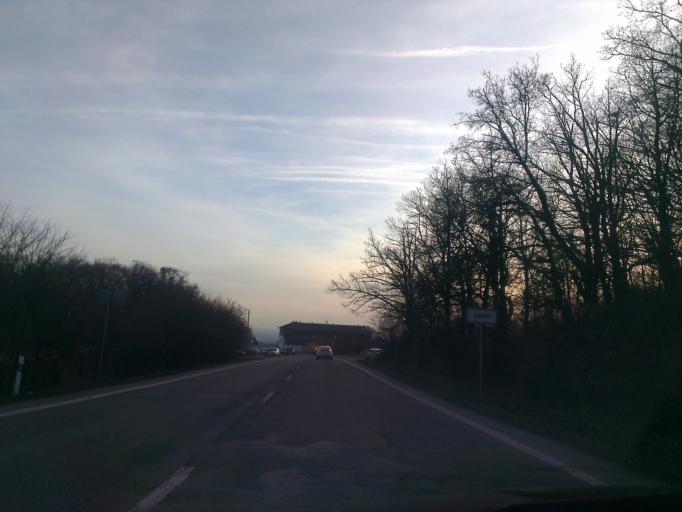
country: CZ
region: South Moravian
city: Bilovice nad Svitavou
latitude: 49.2189
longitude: 16.6818
